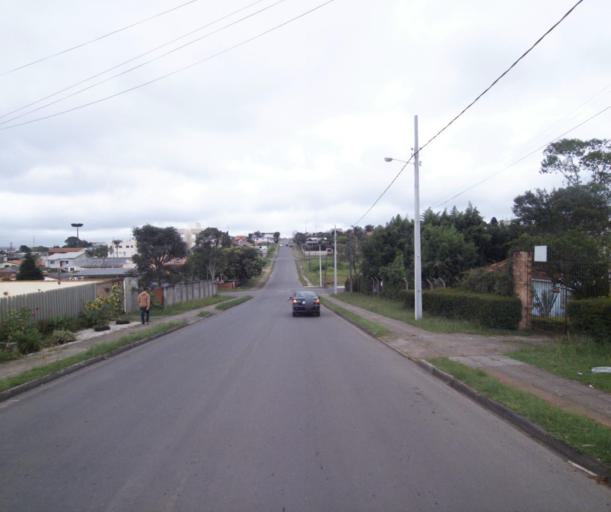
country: BR
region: Parana
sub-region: Quatro Barras
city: Quatro Barras
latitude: -25.3630
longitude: -49.1078
